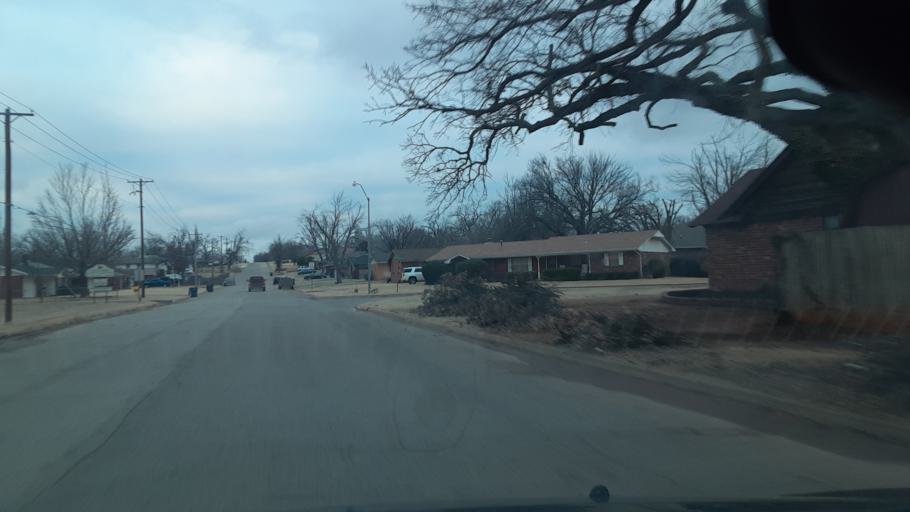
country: US
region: Oklahoma
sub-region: Logan County
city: Guthrie
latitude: 35.8876
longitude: -97.4164
